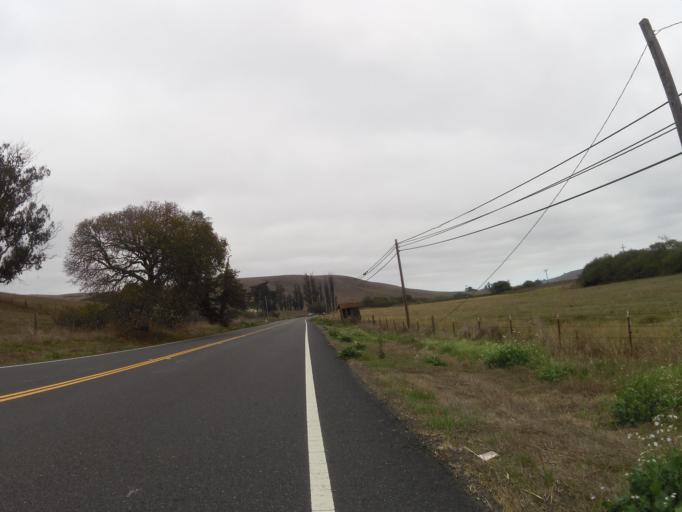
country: US
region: California
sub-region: Sonoma County
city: Occidental
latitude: 38.3210
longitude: -122.9162
